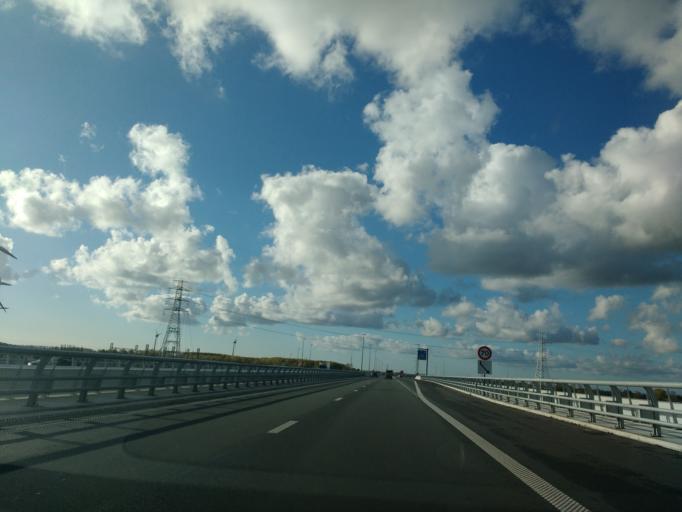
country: BE
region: Flanders
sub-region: Provincie West-Vlaanderen
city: Zuienkerke
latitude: 51.2690
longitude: 3.2020
